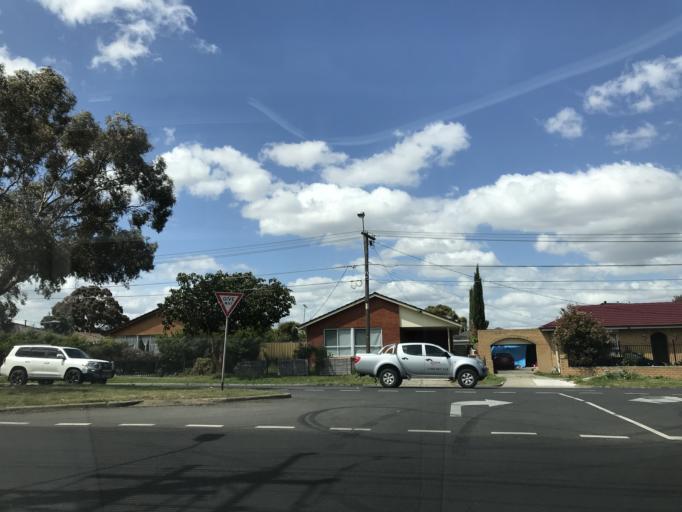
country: AU
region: Victoria
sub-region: Brimbank
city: Sunshine West
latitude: -37.7967
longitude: 144.8182
